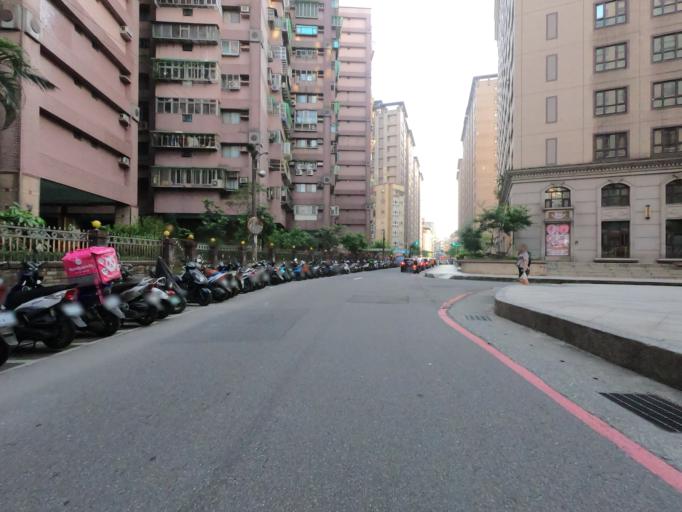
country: TW
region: Taipei
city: Taipei
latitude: 25.0693
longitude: 121.6387
